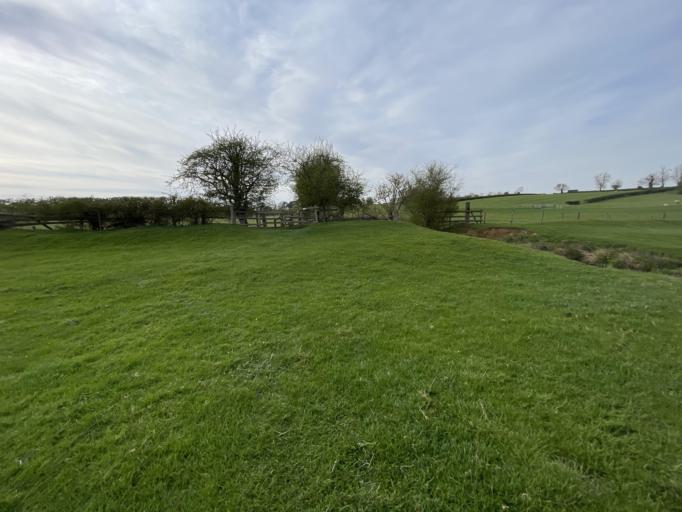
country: GB
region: England
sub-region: Northamptonshire
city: Long Buckby
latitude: 52.4169
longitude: -1.0411
